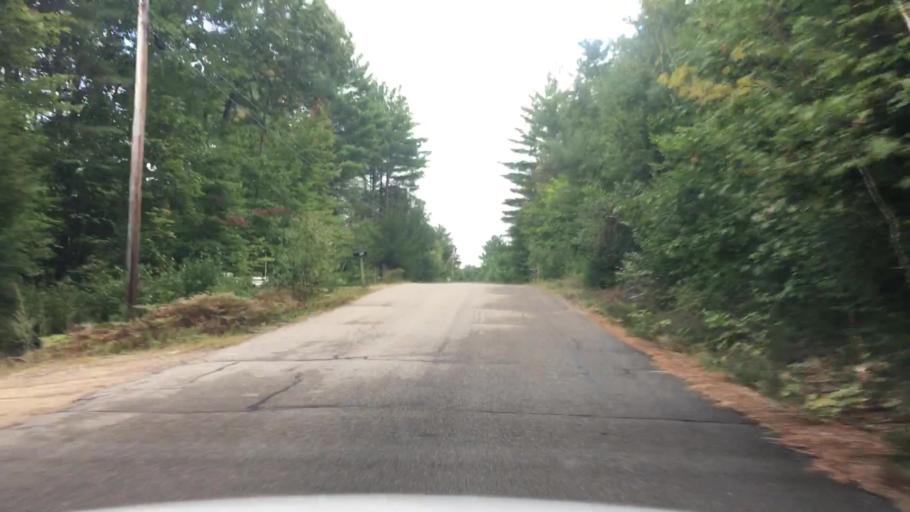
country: US
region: New Hampshire
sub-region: Carroll County
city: Effingham
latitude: 43.7743
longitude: -70.9980
